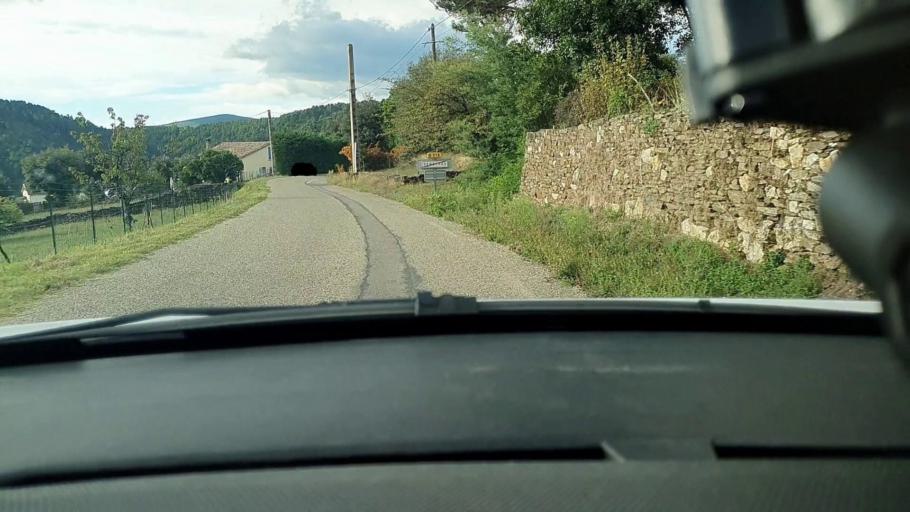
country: FR
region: Languedoc-Roussillon
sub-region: Departement du Gard
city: Besseges
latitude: 44.3264
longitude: 4.0246
